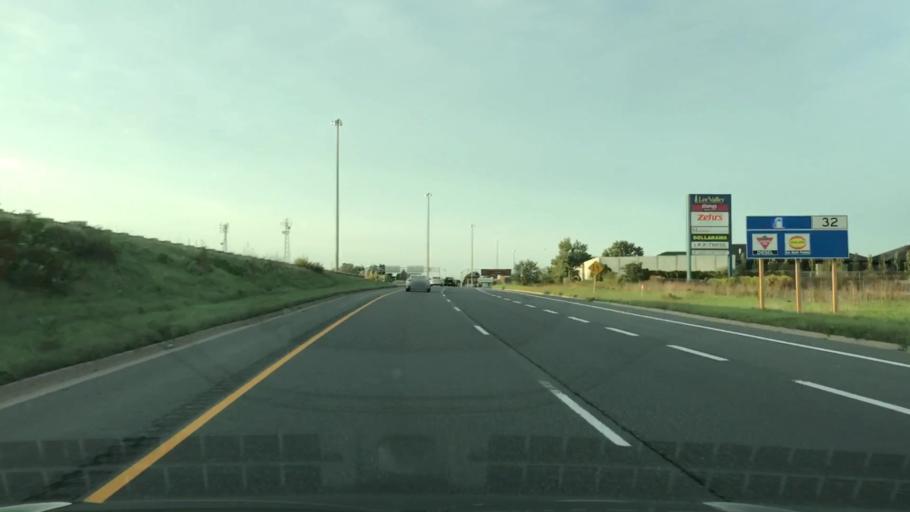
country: CA
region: Ontario
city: Niagara Falls
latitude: 43.1029
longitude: -79.1190
